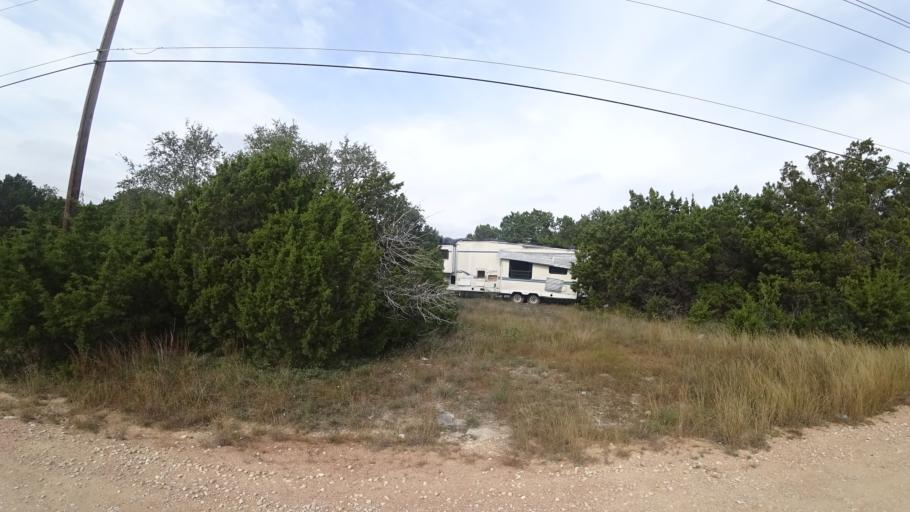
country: US
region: Texas
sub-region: Travis County
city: Hudson Bend
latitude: 30.3930
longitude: -97.9309
